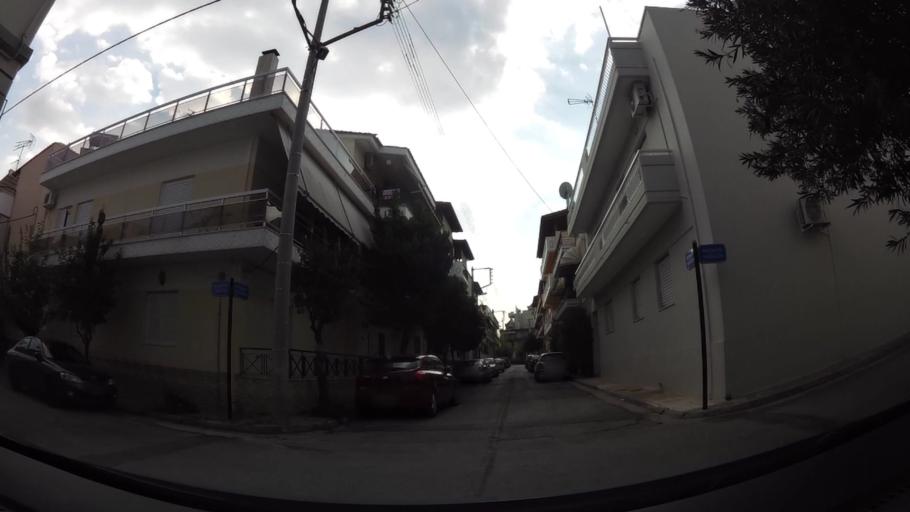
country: GR
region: Attica
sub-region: Nomarchia Athinas
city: Ilion
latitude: 38.0446
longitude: 23.7018
